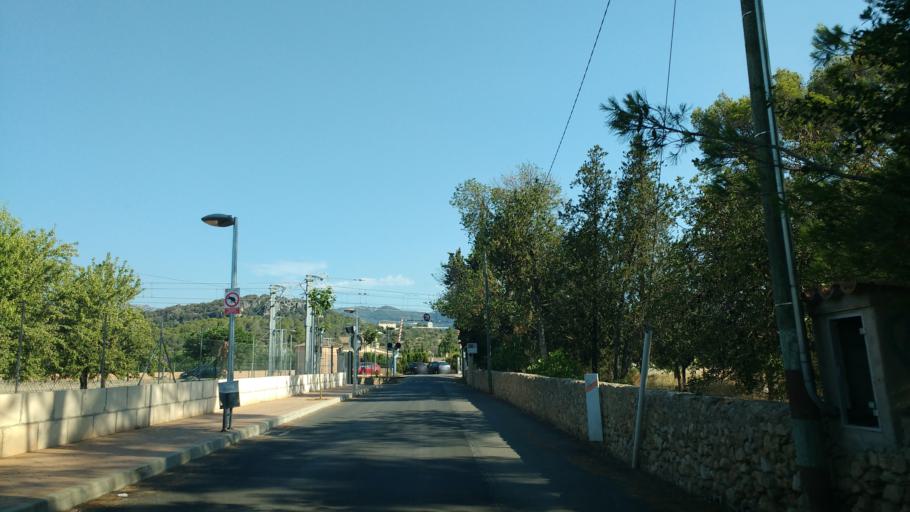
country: ES
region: Balearic Islands
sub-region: Illes Balears
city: Consell
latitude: 39.6776
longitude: 2.8095
